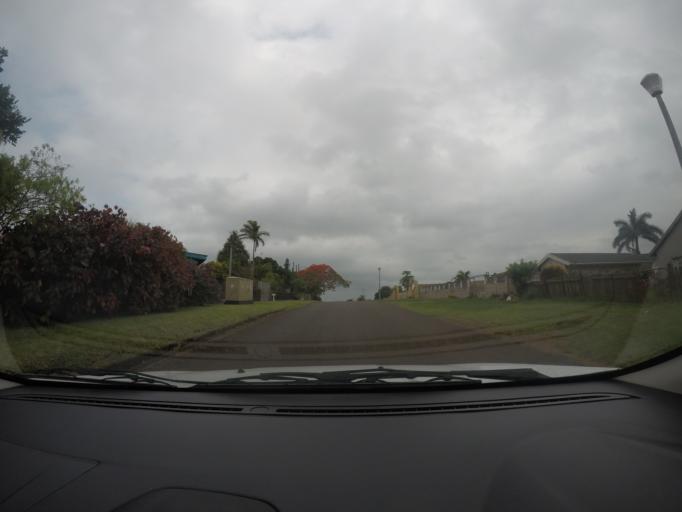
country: ZA
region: KwaZulu-Natal
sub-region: uThungulu District Municipality
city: Empangeni
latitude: -28.7369
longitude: 31.8995
